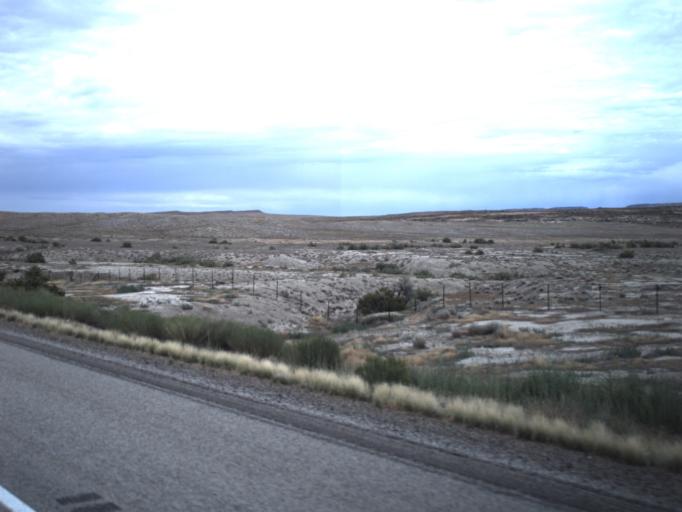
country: US
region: Utah
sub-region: Grand County
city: Moab
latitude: 39.0144
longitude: -109.3040
